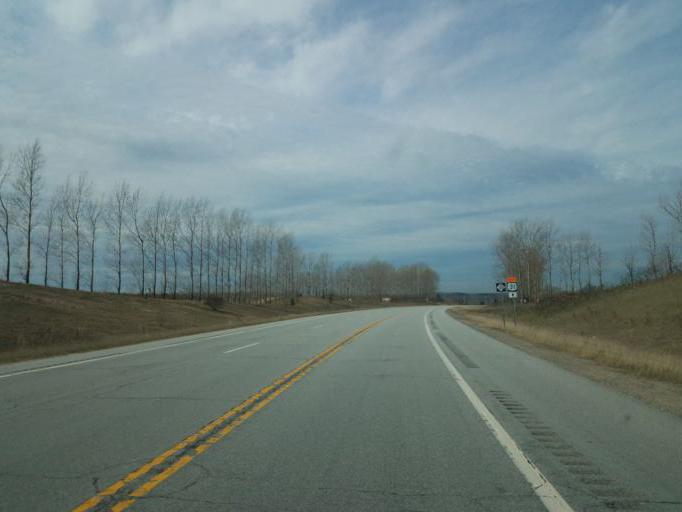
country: US
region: Michigan
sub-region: Oceana County
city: Shelby
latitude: 43.5585
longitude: -86.3725
